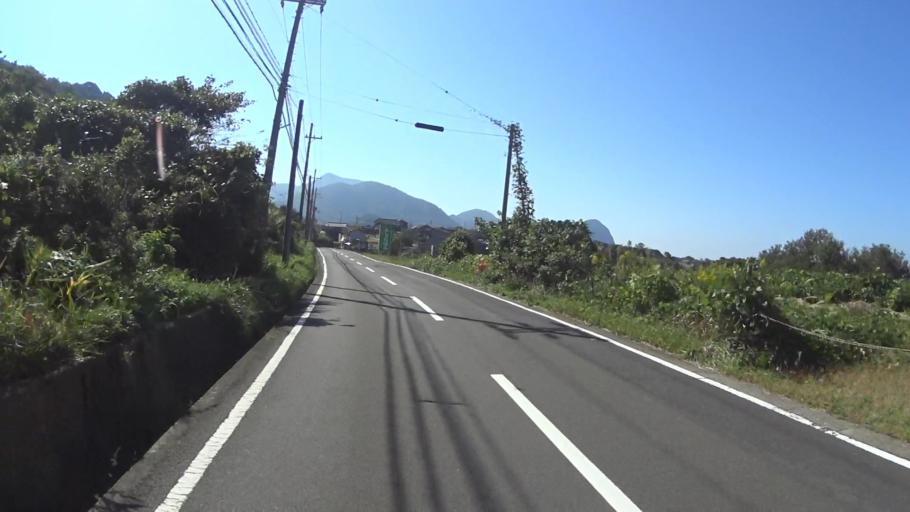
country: JP
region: Kyoto
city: Miyazu
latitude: 35.7609
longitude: 135.1836
